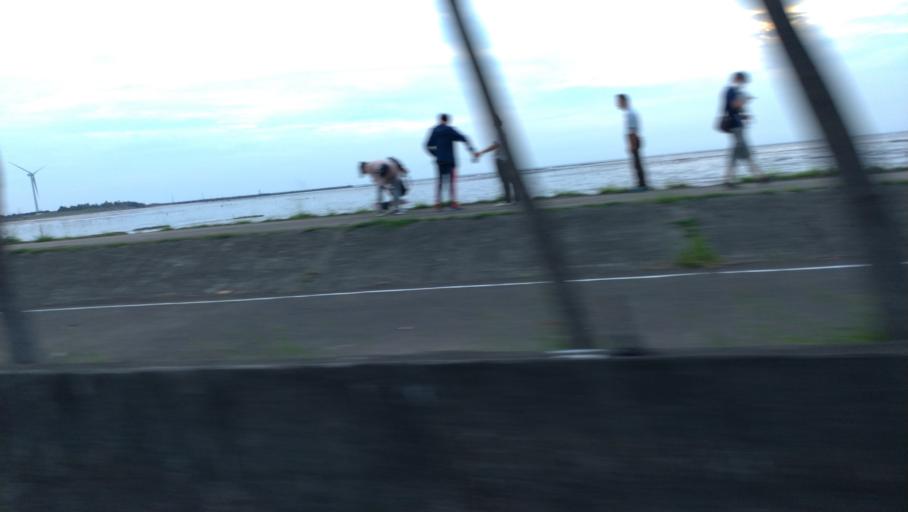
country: TW
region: Taiwan
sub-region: Hsinchu
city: Hsinchu
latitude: 24.7697
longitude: 120.9134
